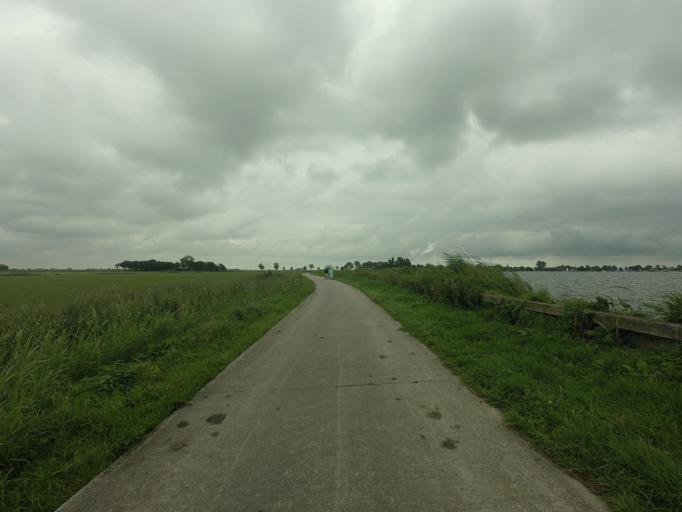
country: NL
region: Friesland
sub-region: Sudwest Fryslan
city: Bolsward
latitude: 52.9979
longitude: 5.5387
